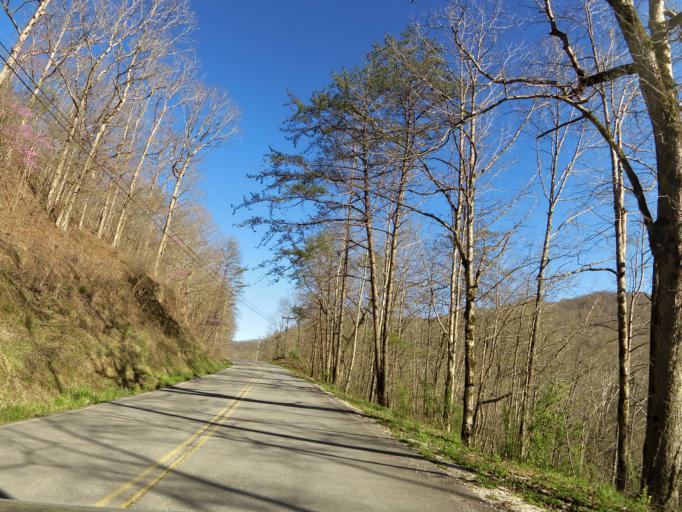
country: US
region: Tennessee
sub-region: Scott County
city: Huntsville
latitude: 36.2985
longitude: -84.3854
